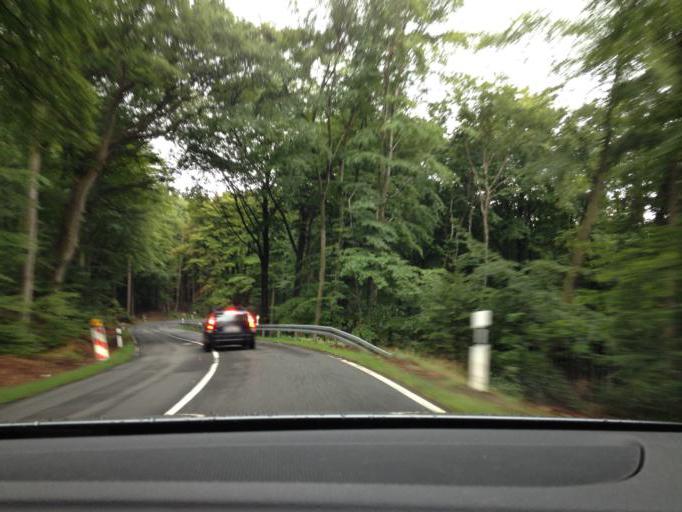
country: DE
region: Hesse
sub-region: Regierungsbezirk Darmstadt
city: Schlangenbad
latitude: 50.1022
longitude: 8.1420
